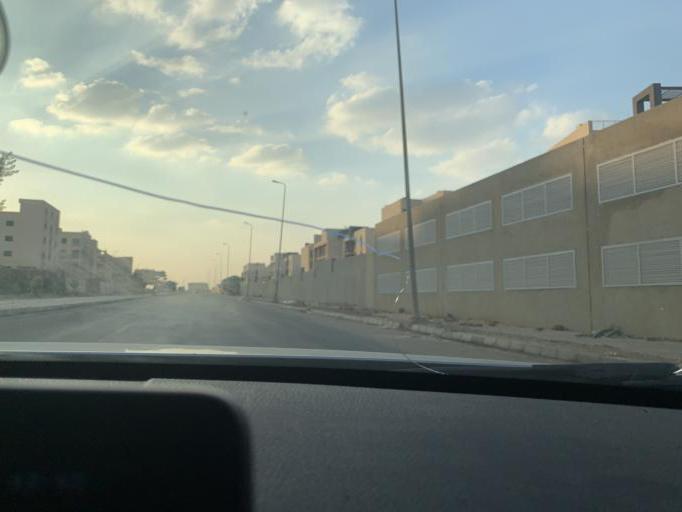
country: EG
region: Muhafazat al Qalyubiyah
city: Al Khankah
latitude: 30.0188
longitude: 31.4789
